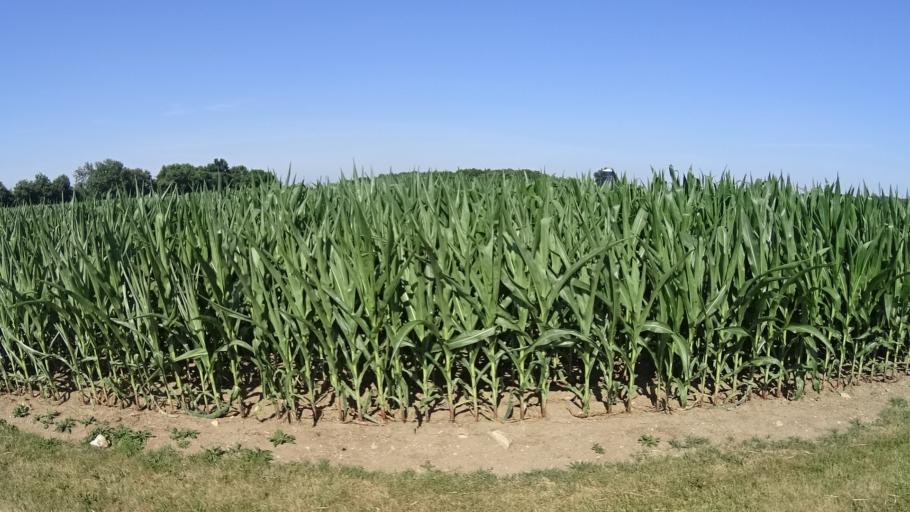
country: US
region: Ohio
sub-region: Huron County
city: Bellevue
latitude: 41.3690
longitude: -82.8191
